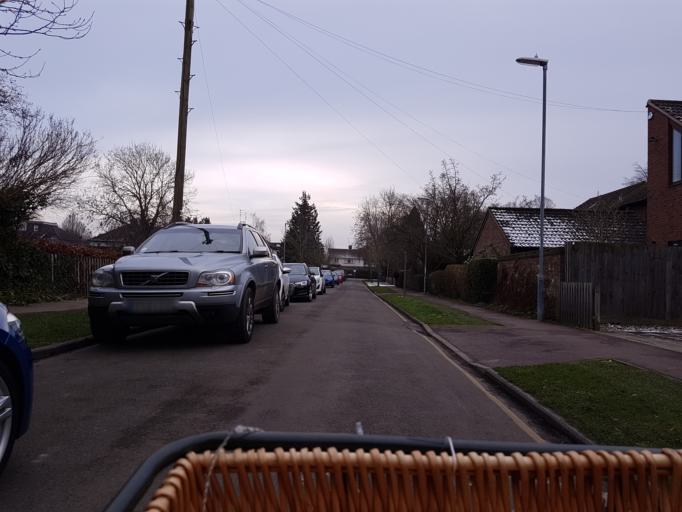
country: GB
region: England
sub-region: Cambridgeshire
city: Cambridge
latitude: 52.1836
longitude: 0.1453
